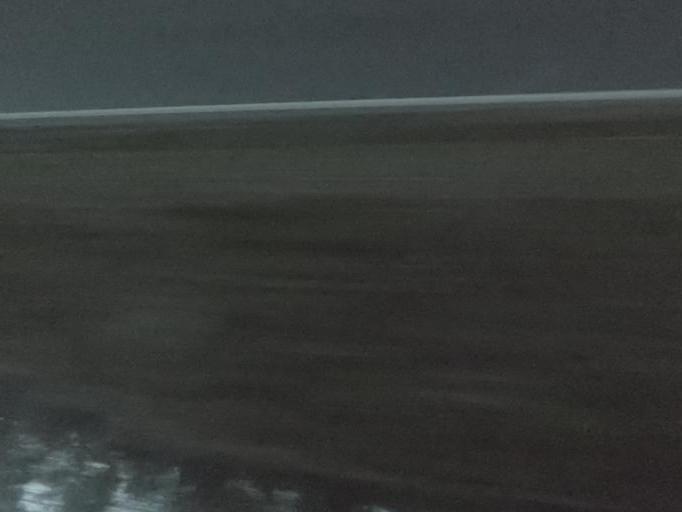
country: PT
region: Porto
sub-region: Baiao
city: Valadares
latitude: 41.2173
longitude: -7.9842
